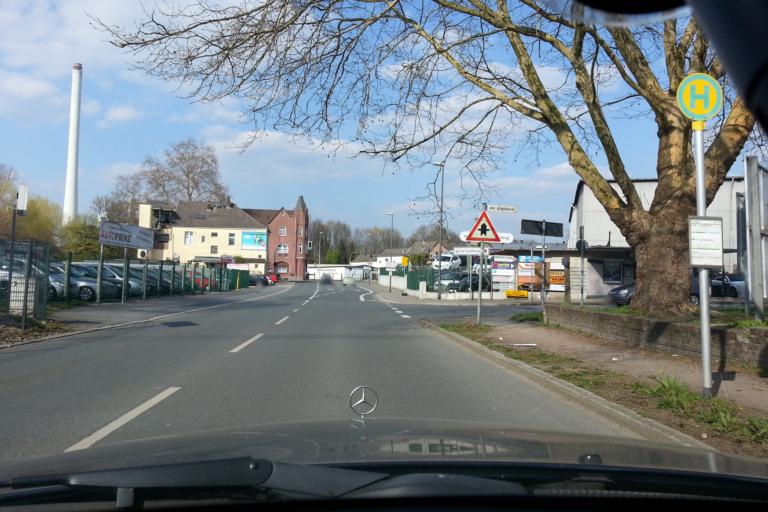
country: DE
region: North Rhine-Westphalia
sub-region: Regierungsbezirk Arnsberg
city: Herne
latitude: 51.5415
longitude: 7.1900
